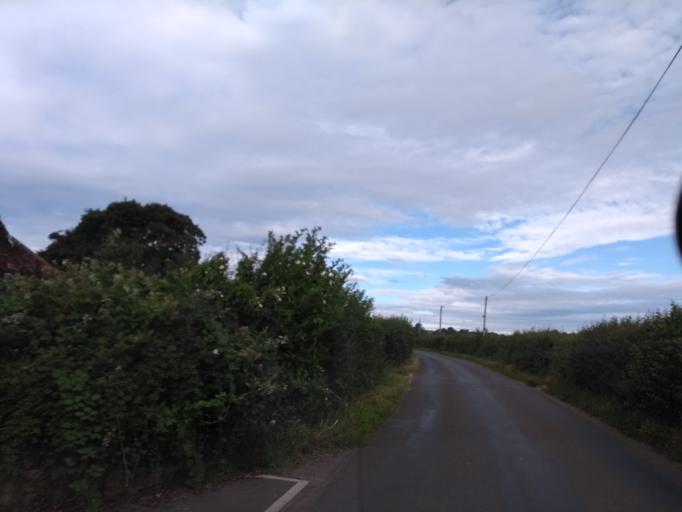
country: GB
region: England
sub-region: Somerset
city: Crewkerne
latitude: 50.8711
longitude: -2.7838
